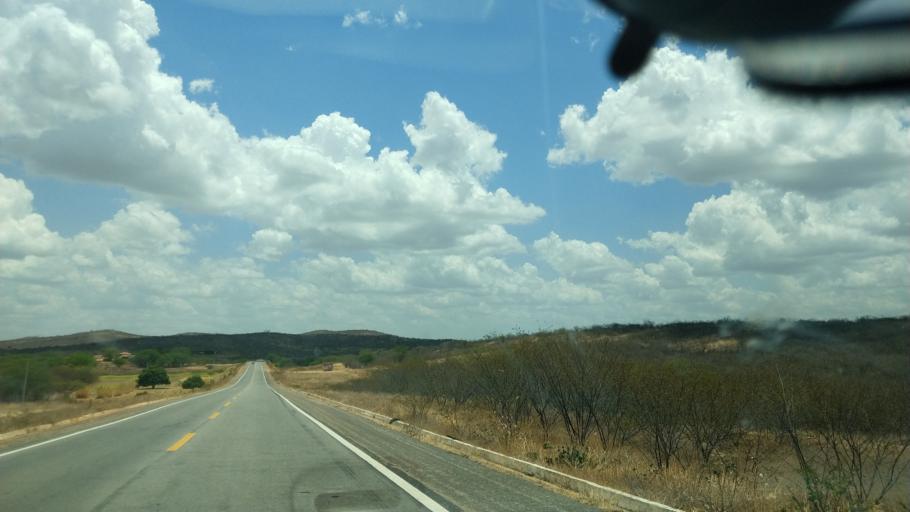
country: BR
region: Rio Grande do Norte
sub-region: Currais Novos
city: Currais Novos
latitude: -6.2516
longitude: -36.4755
